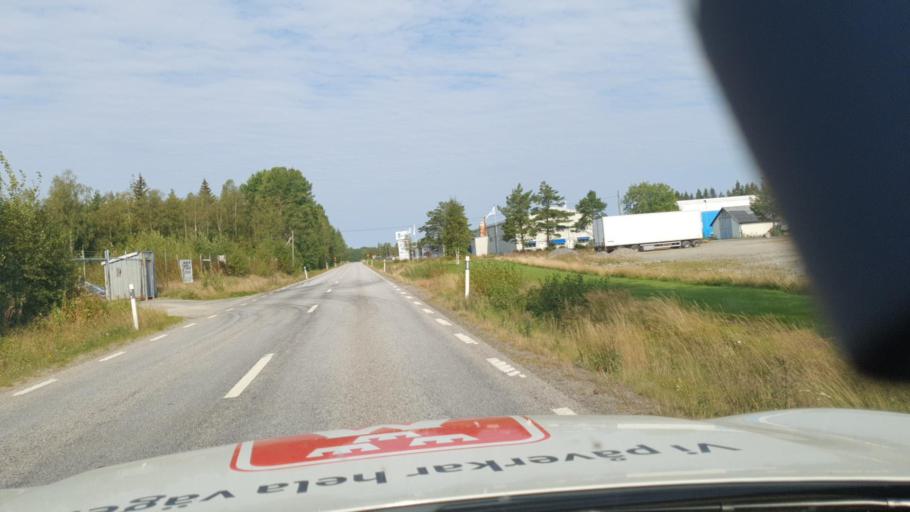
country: SE
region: Vaestra Goetaland
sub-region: Dals-Ed Kommun
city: Ed
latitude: 58.8891
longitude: 11.9760
